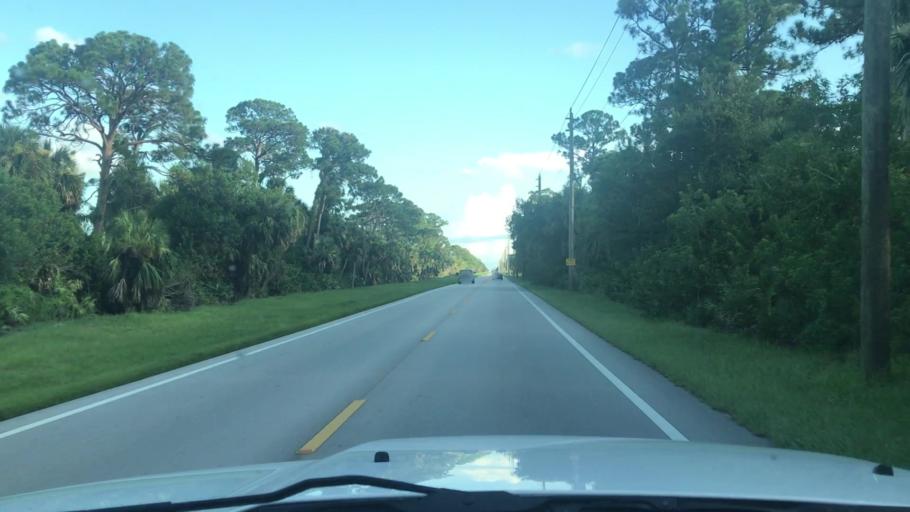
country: US
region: Florida
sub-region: Indian River County
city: Winter Beach
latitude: 27.7291
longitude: -80.4624
